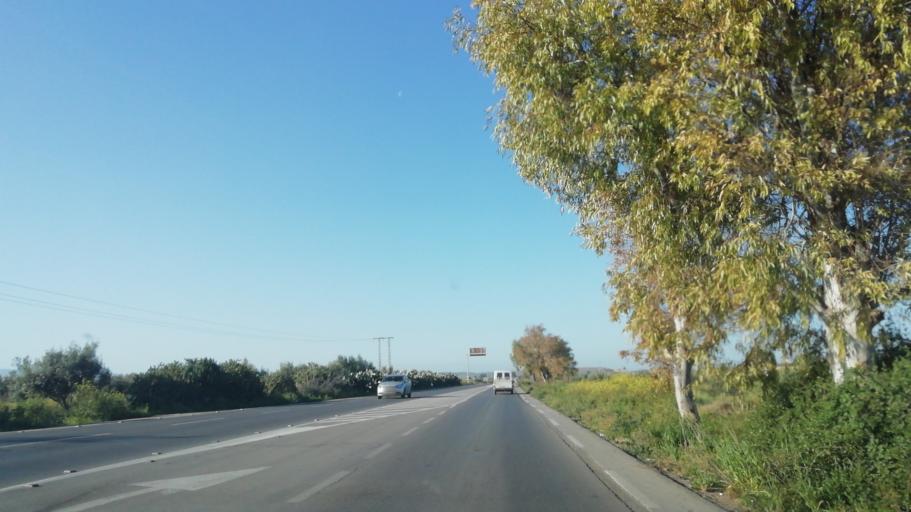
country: DZ
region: Mascara
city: Mascara
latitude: 35.6594
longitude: 0.1968
